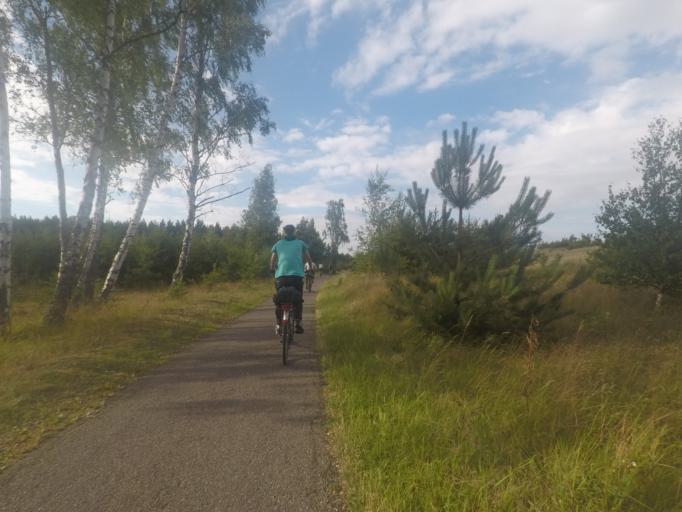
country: LT
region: Klaipedos apskritis
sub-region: Klaipeda
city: Klaipeda
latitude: 55.6335
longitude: 21.1163
